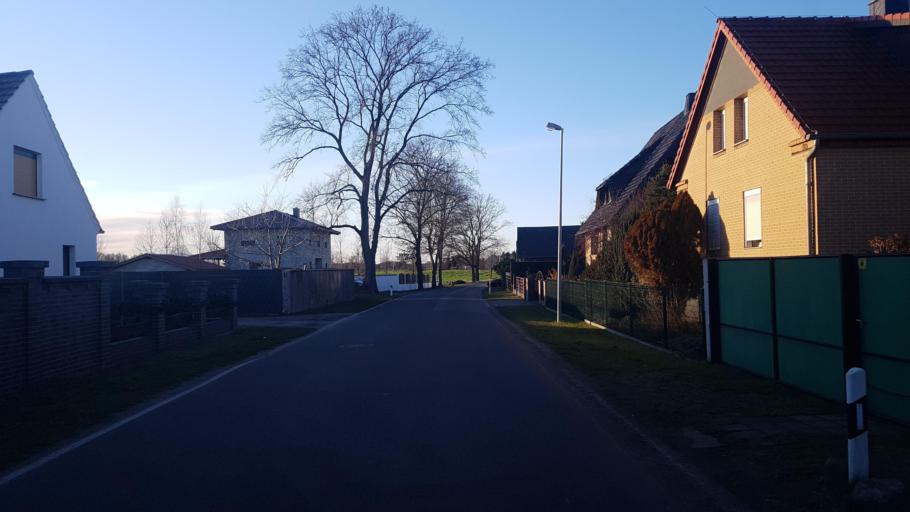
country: DE
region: Brandenburg
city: Drehnow
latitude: 51.8669
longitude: 14.3490
